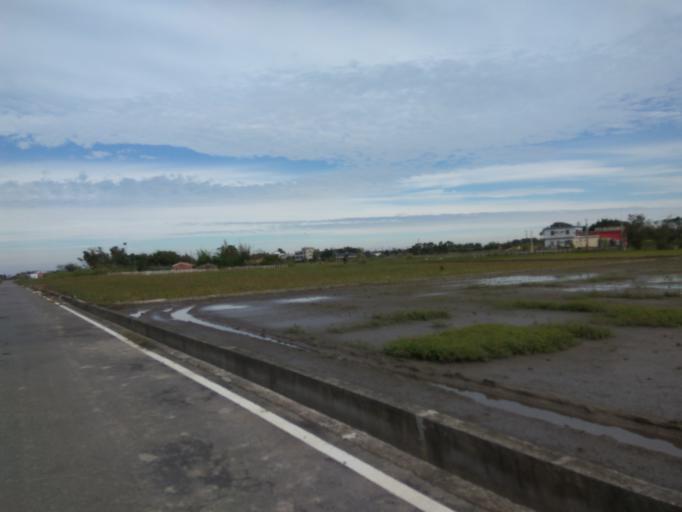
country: TW
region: Taiwan
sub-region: Hsinchu
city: Zhubei
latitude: 24.9493
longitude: 121.1061
